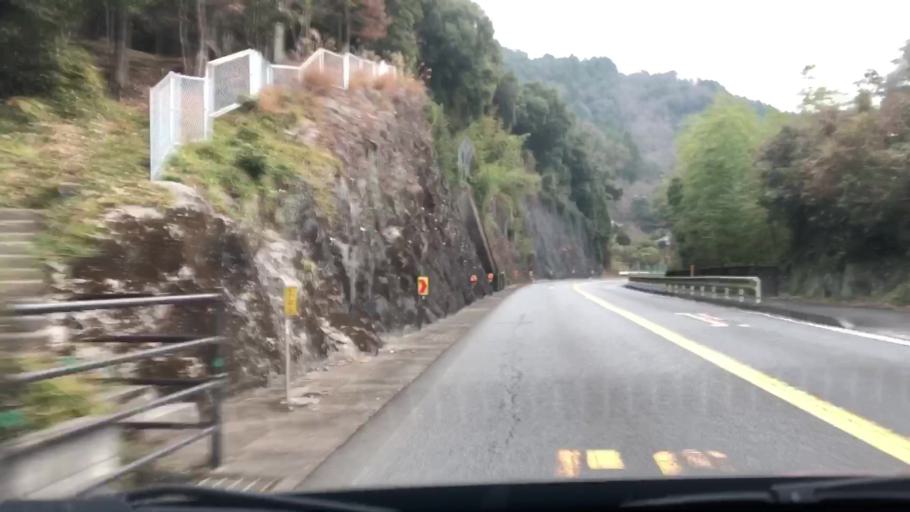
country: JP
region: Oita
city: Usuki
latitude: 33.0102
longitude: 131.7060
